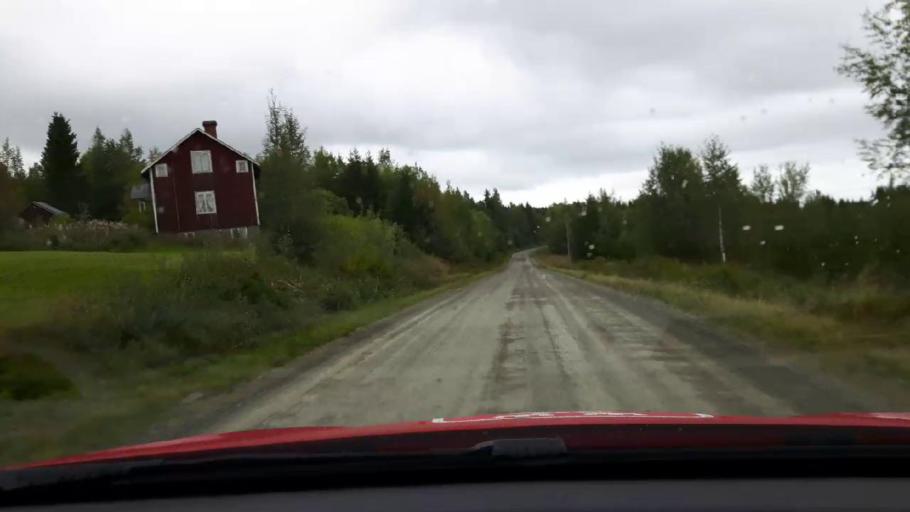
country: SE
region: Jaemtland
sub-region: Bergs Kommun
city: Hoverberg
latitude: 62.8713
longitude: 14.3006
